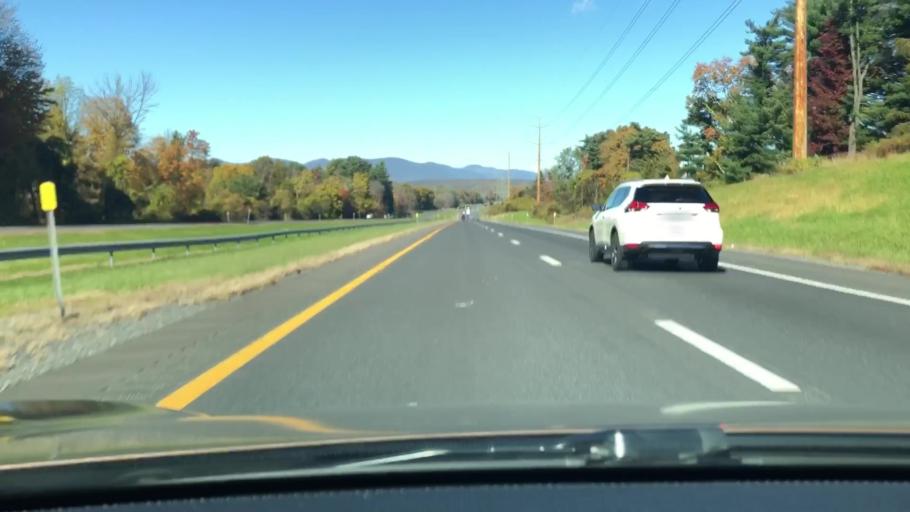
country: US
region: New York
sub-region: Ulster County
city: Hurley
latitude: 41.9095
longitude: -74.0428
